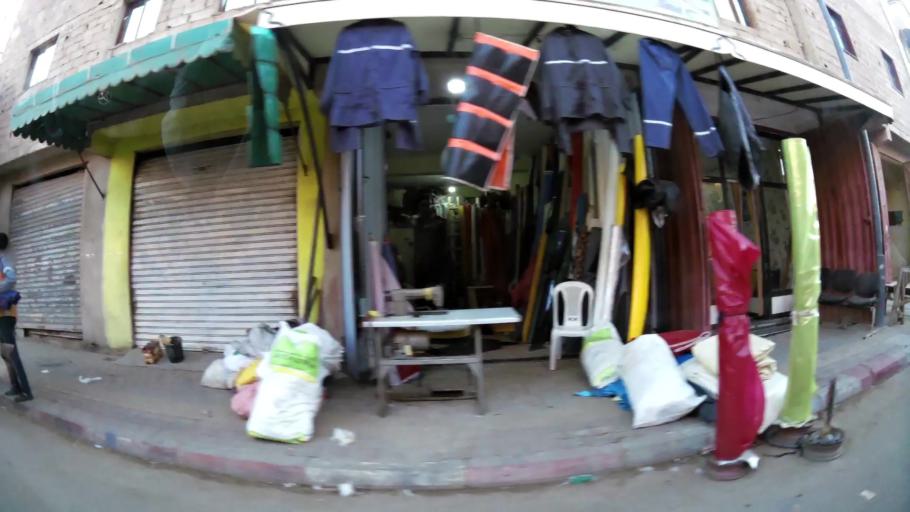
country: MA
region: Marrakech-Tensift-Al Haouz
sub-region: Kelaa-Des-Sraghna
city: Sidi Abdallah
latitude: 32.2422
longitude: -7.9542
